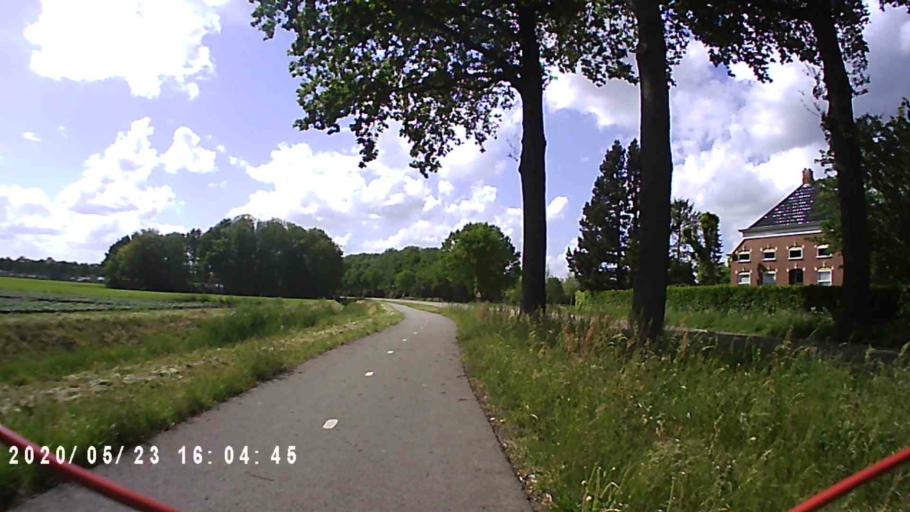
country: NL
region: Groningen
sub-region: Gemeente Appingedam
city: Appingedam
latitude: 53.2452
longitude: 6.8963
